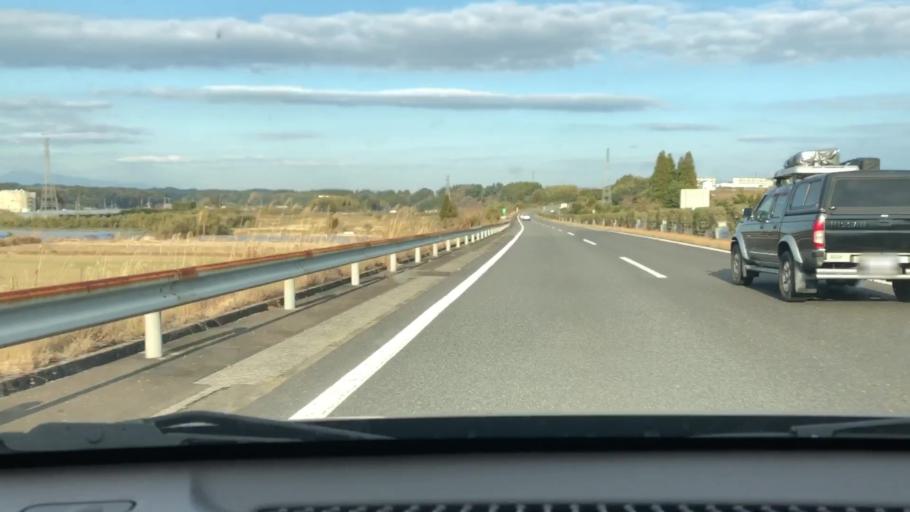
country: JP
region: Miyazaki
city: Miyazaki-shi
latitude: 31.8248
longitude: 131.3081
